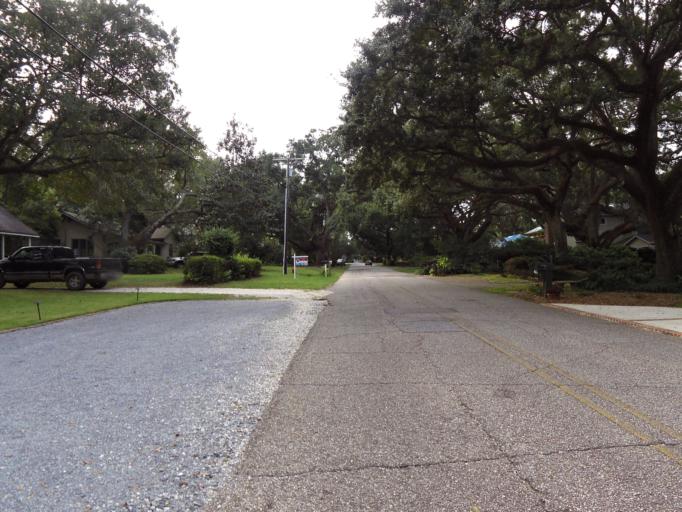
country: US
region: Alabama
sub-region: Baldwin County
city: Fairhope
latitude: 30.5261
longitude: -87.9063
